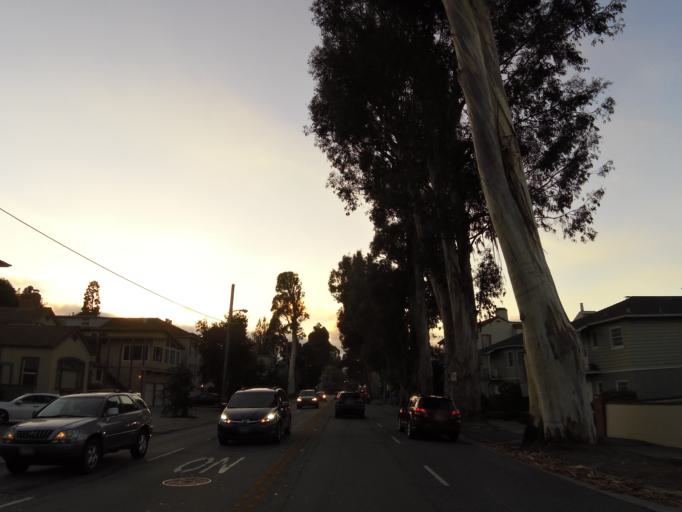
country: US
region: California
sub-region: San Mateo County
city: Burlingame
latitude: 37.5832
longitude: -122.3645
